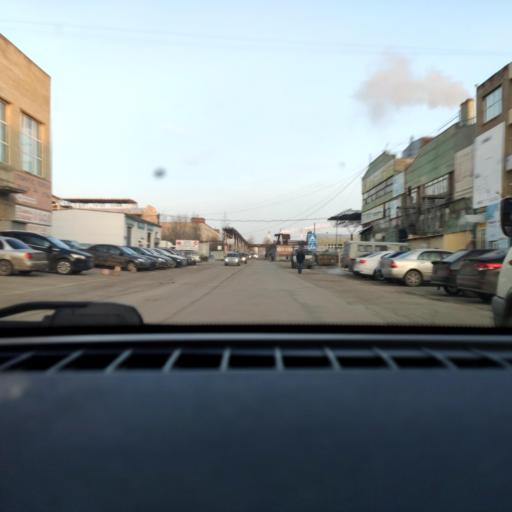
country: RU
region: Perm
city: Froly
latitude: 57.9608
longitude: 56.2738
